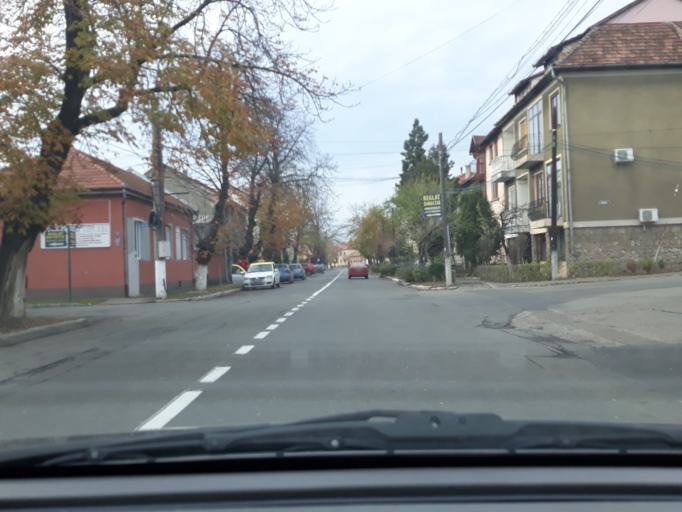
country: RO
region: Bihor
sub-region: Comuna Biharea
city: Oradea
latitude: 47.0454
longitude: 21.9476
